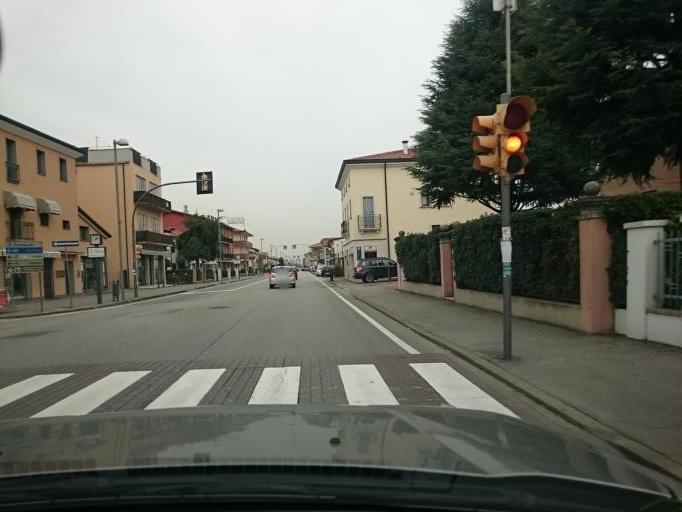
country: IT
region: Veneto
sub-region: Provincia di Padova
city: Albignasego
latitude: 45.3479
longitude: 11.8681
